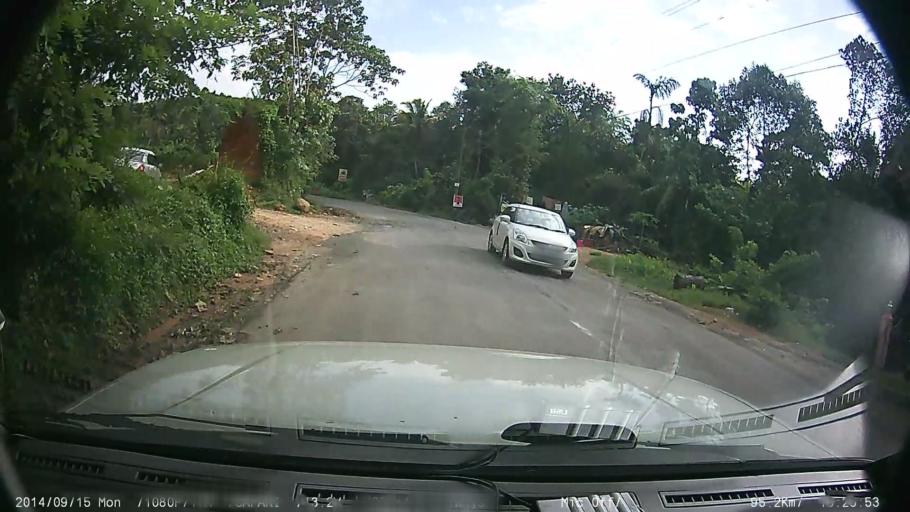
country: IN
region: Kerala
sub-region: Ernakulam
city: Piravam
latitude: 9.8852
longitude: 76.5918
